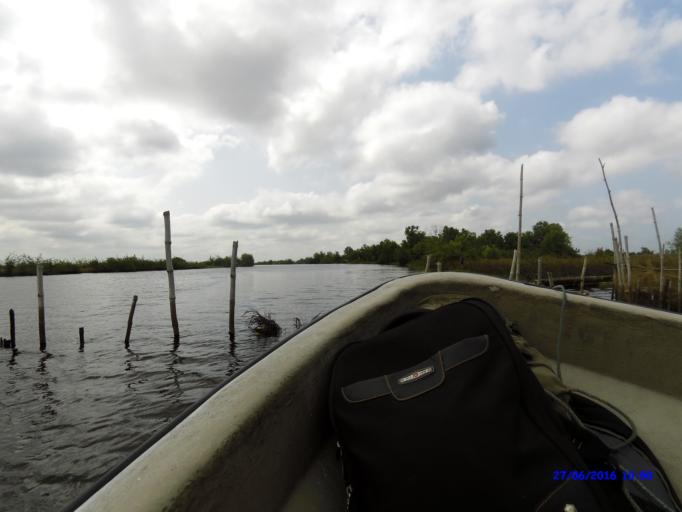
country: BJ
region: Mono
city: Come
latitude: 6.3683
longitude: 1.9290
